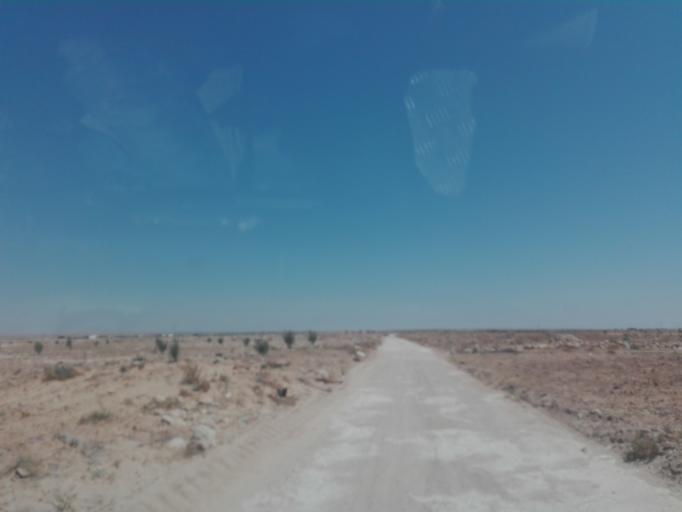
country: TN
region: Safaqis
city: Skhira
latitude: 34.3972
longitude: 9.9281
